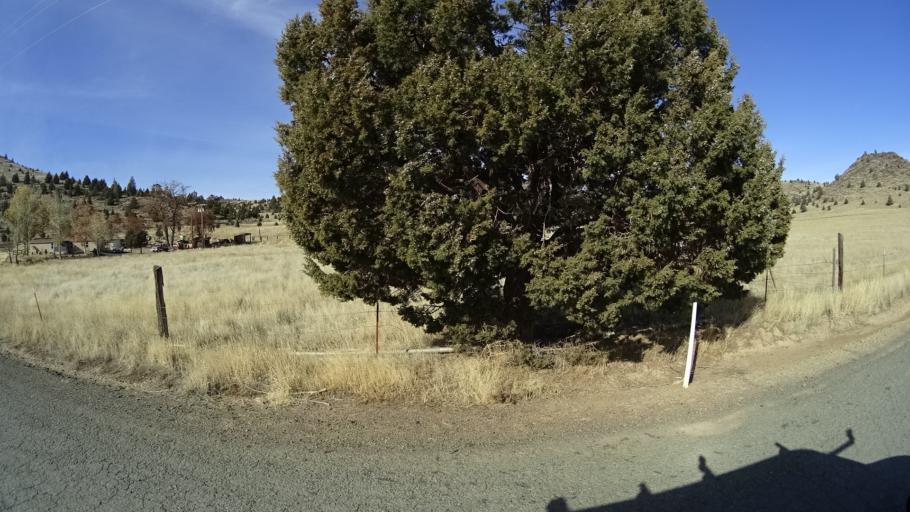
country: US
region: California
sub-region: Siskiyou County
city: Weed
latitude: 41.5601
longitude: -122.4706
